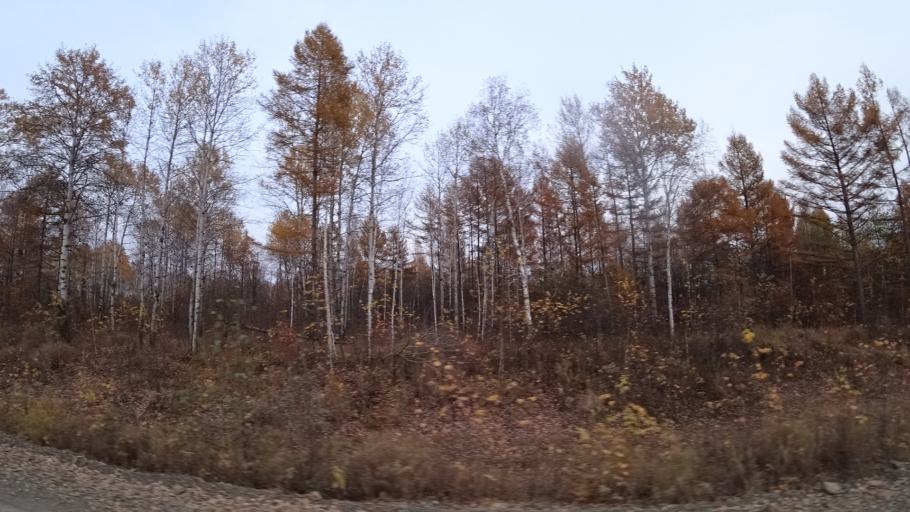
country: RU
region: Khabarovsk Krai
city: Amursk
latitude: 49.9824
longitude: 136.3148
